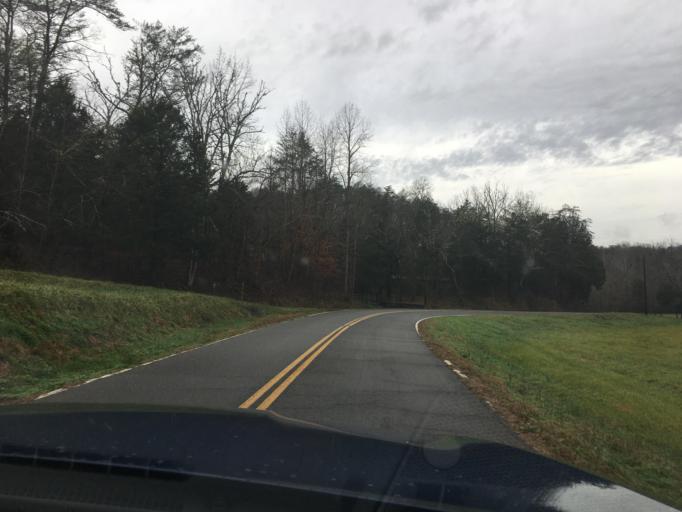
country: US
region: Tennessee
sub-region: McMinn County
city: Englewood
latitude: 35.3643
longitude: -84.4286
